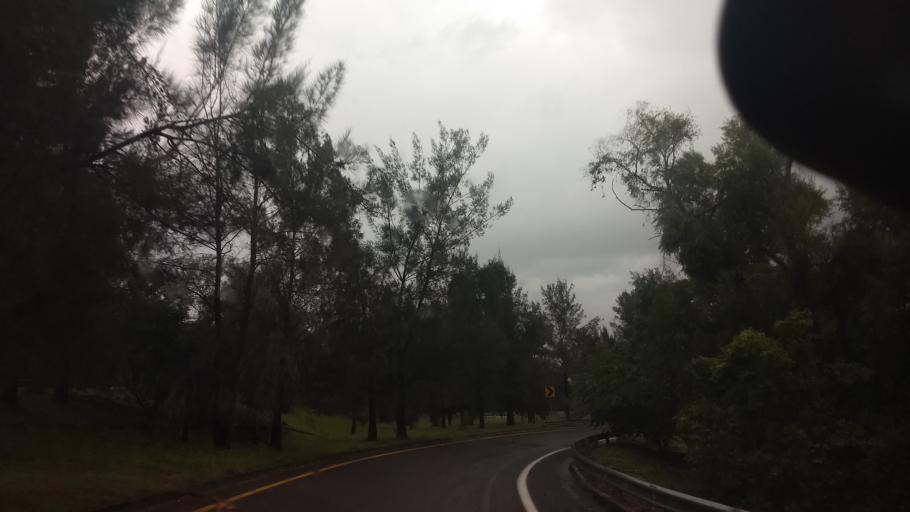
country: MX
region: Colima
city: Cofradia
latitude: 19.4004
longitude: -103.5368
